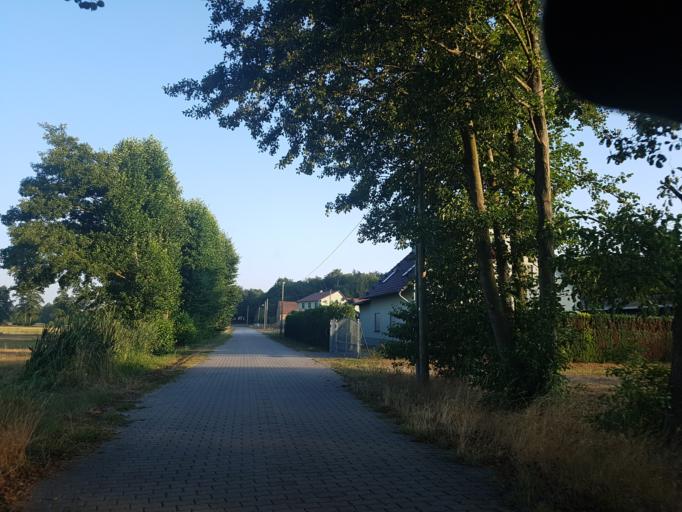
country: DE
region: Brandenburg
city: Falkenberg
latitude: 51.6428
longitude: 13.2946
